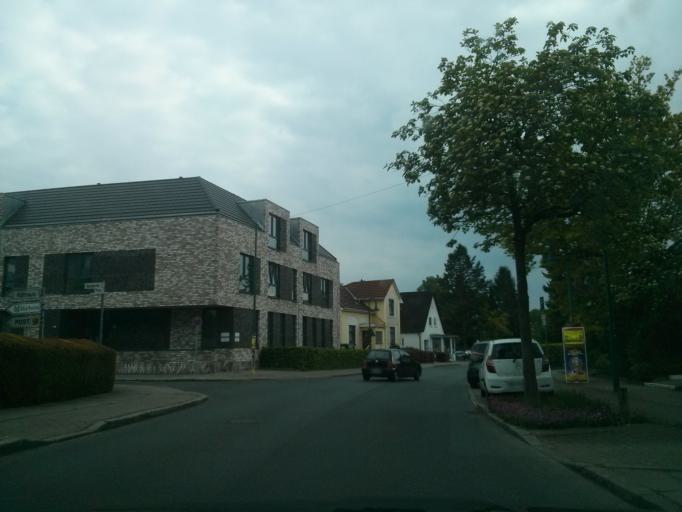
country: DE
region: Schleswig-Holstein
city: Halstenbek
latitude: 53.6353
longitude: 9.8395
